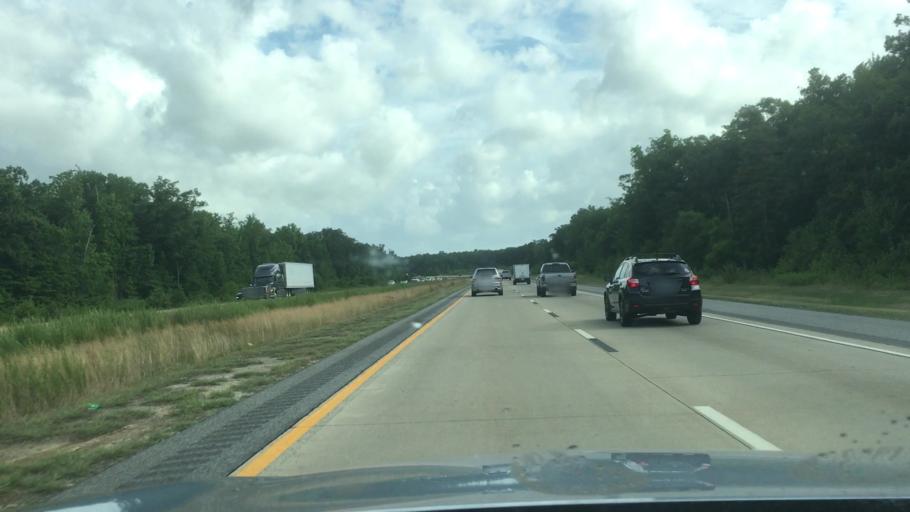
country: US
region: Delaware
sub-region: New Castle County
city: Townsend
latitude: 39.4011
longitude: -75.6650
